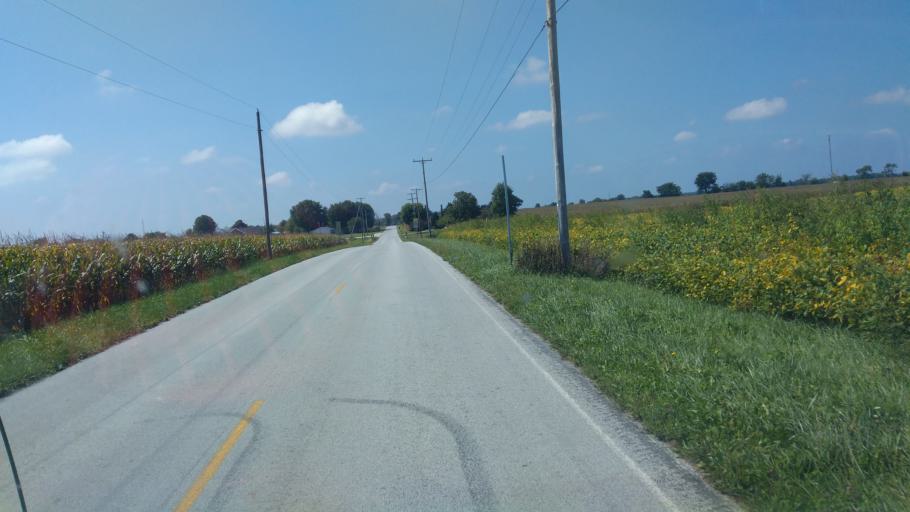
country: US
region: Ohio
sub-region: Hardin County
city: Kenton
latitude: 40.6667
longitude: -83.5955
